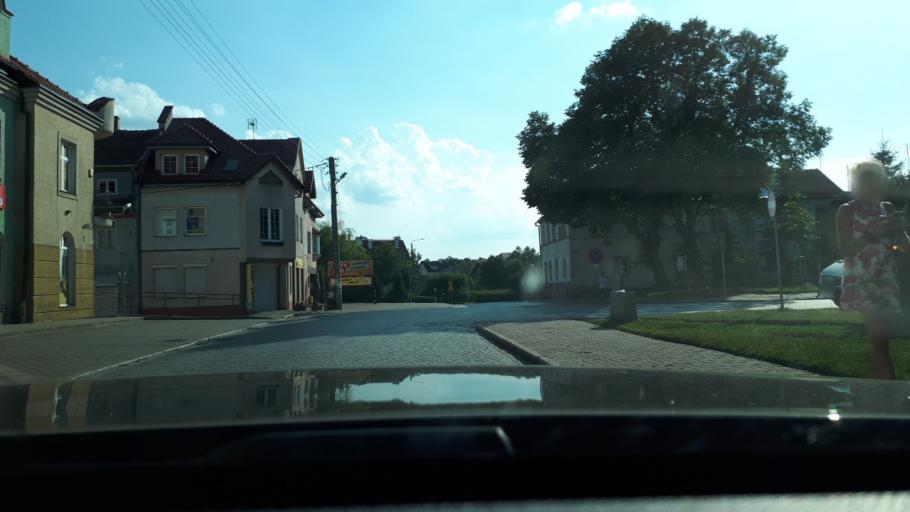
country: PL
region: Warmian-Masurian Voivodeship
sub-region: Powiat olsztynski
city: Olsztynek
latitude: 53.5819
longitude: 20.2820
